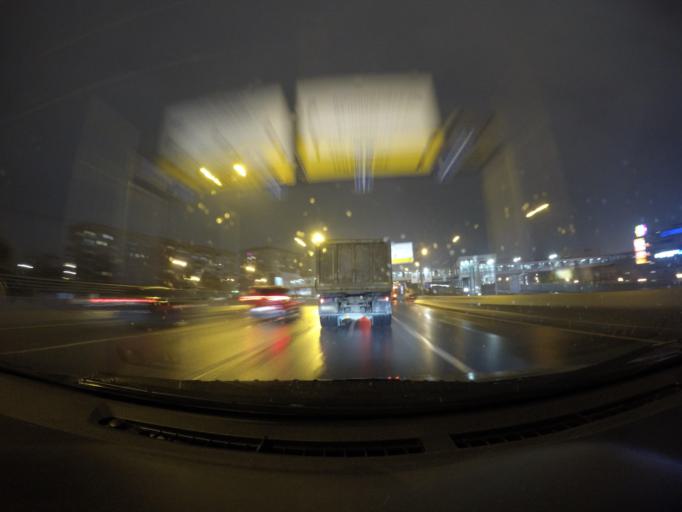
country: RU
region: Moskovskaya
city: Kozhukhovo
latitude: 55.7118
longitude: 37.6740
